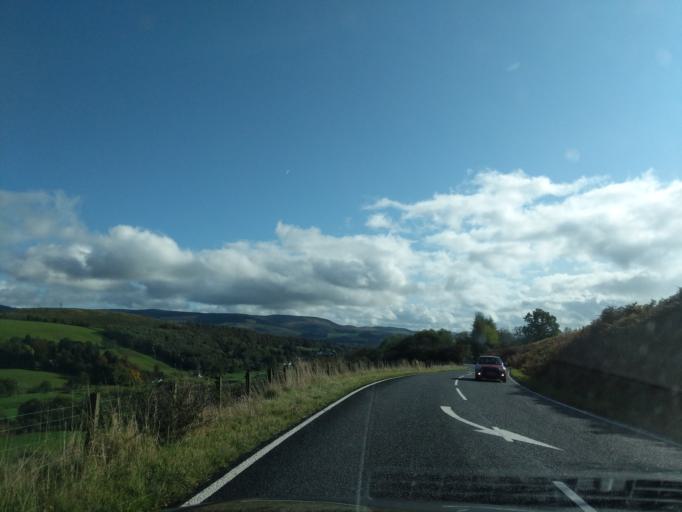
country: GB
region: Scotland
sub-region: Dumfries and Galloway
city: Moffat
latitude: 55.3520
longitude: -3.4653
